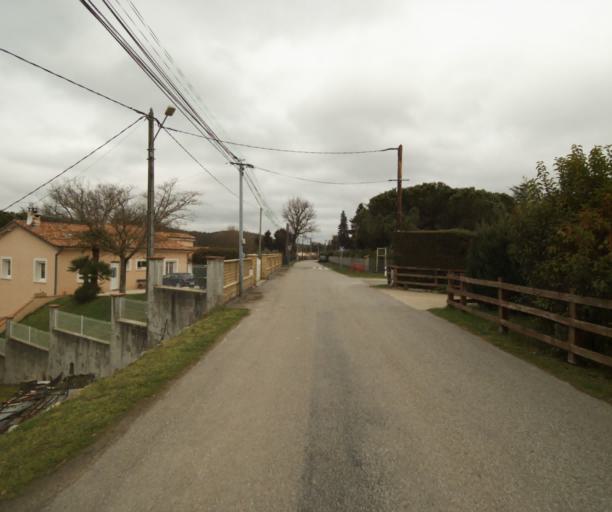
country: FR
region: Midi-Pyrenees
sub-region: Departement de l'Ariege
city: Pamiers
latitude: 43.1335
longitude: 1.6041
